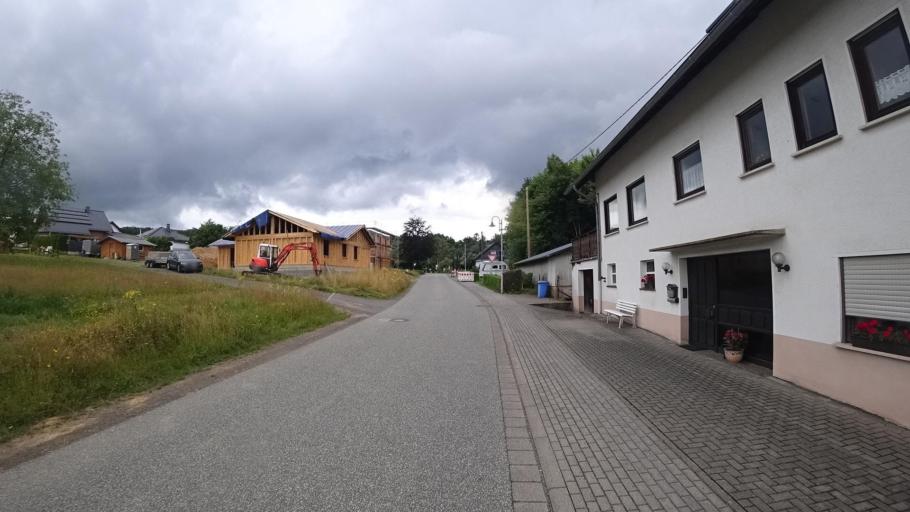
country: DE
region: Rheinland-Pfalz
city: Fiersbach
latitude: 50.7085
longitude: 7.5051
